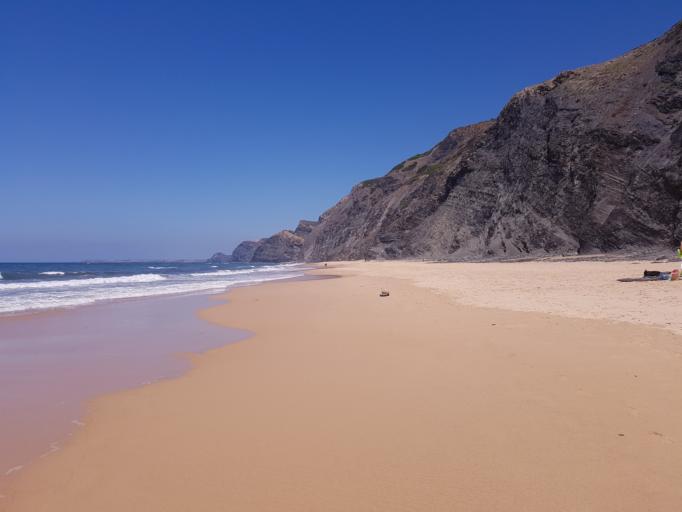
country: PT
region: Faro
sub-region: Vila do Bispo
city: Vila do Bispo
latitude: 37.1124
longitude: -8.9352
